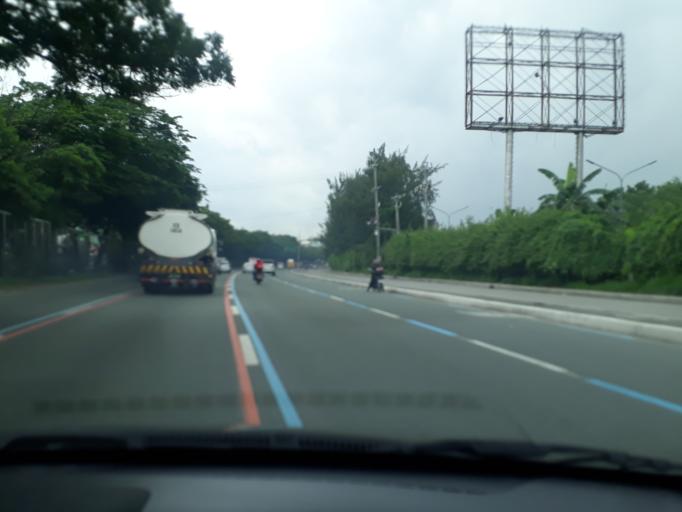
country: PH
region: Calabarzon
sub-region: Province of Rizal
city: Pateros
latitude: 14.5225
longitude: 121.0544
